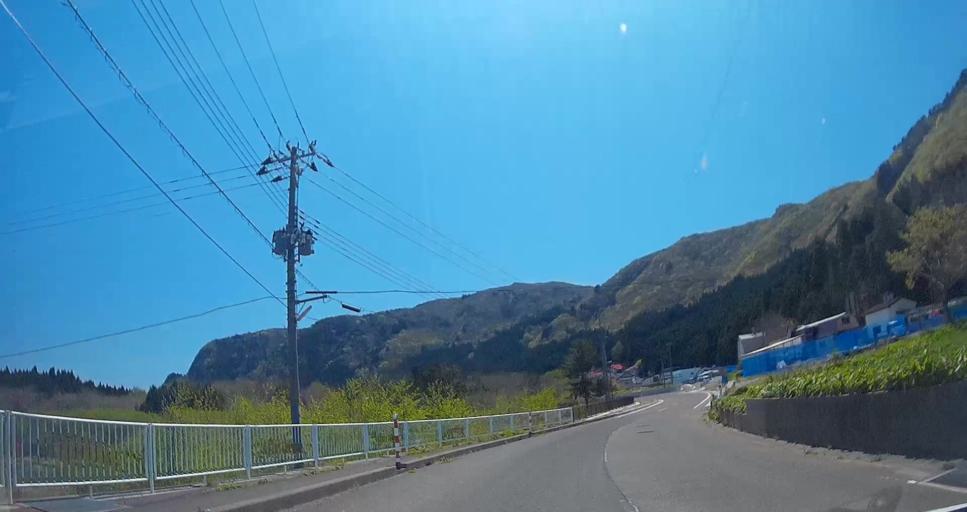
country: JP
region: Aomori
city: Mutsu
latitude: 41.4025
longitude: 141.4467
